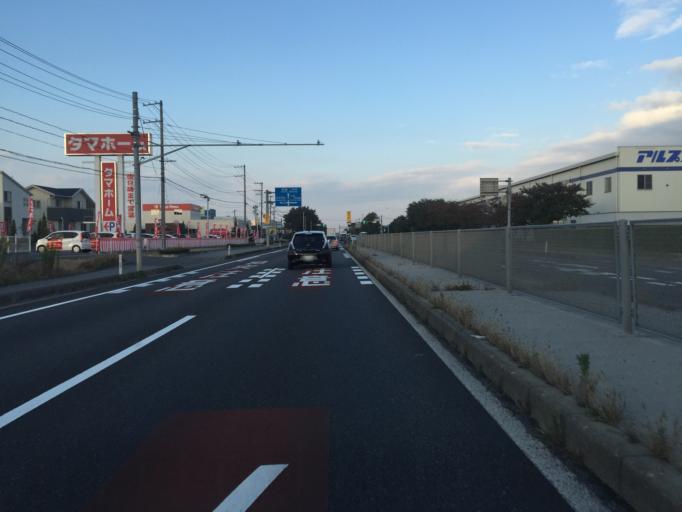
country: JP
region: Fukushima
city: Motomiya
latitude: 37.4902
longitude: 140.3822
